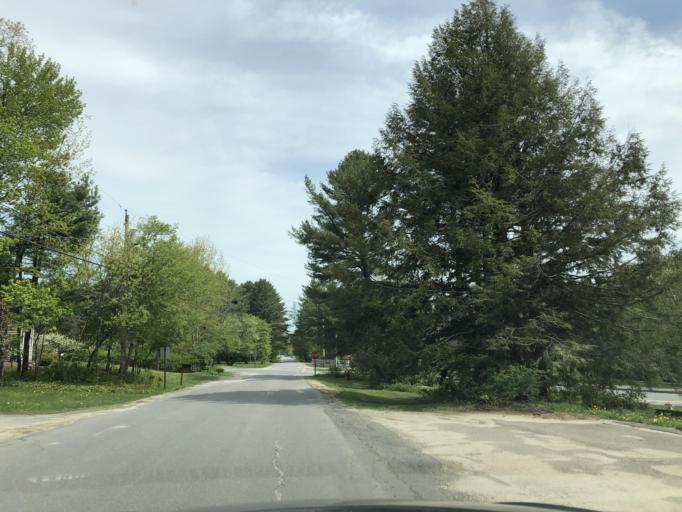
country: US
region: New Hampshire
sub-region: Merrimack County
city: New London
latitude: 43.4173
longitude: -71.9913
